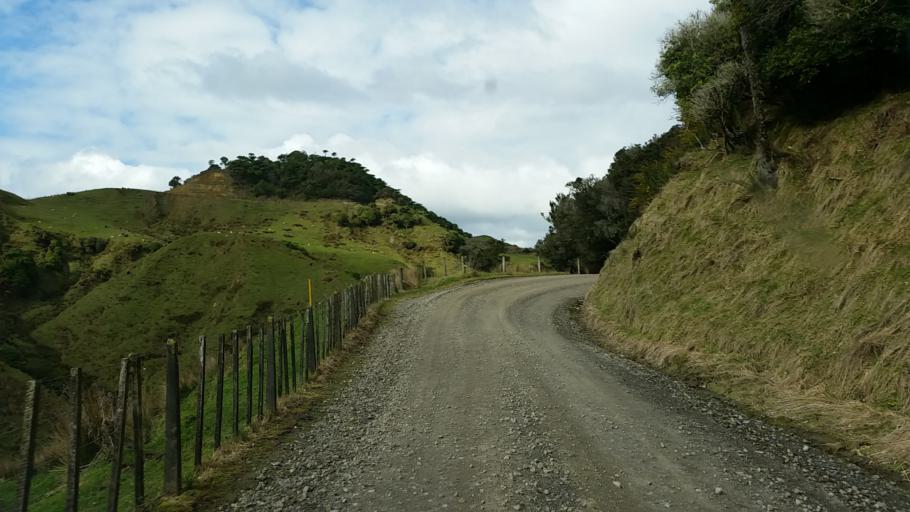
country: NZ
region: Taranaki
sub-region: South Taranaki District
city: Eltham
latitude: -39.1710
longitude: 174.6138
